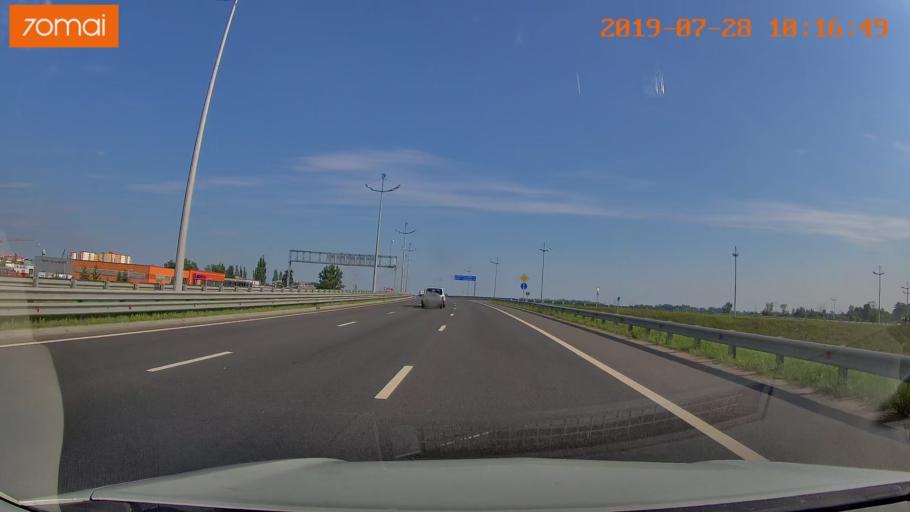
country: RU
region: Kaliningrad
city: Maloye Isakovo
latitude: 54.7312
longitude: 20.5980
